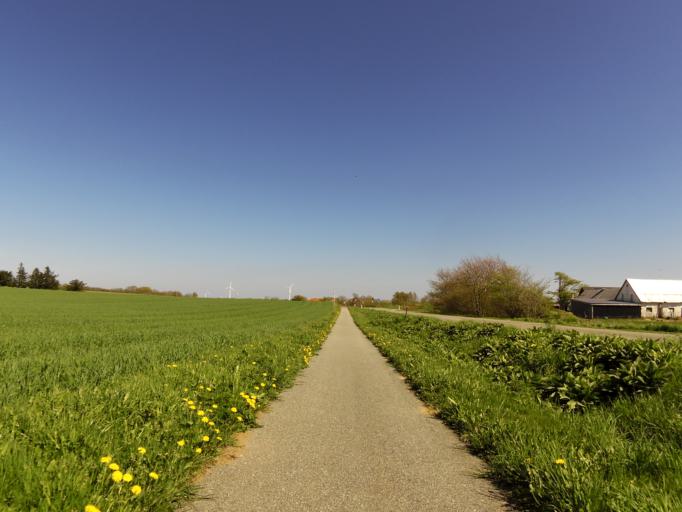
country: DK
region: Central Jutland
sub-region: Holstebro Kommune
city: Vinderup
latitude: 56.6003
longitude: 8.7513
